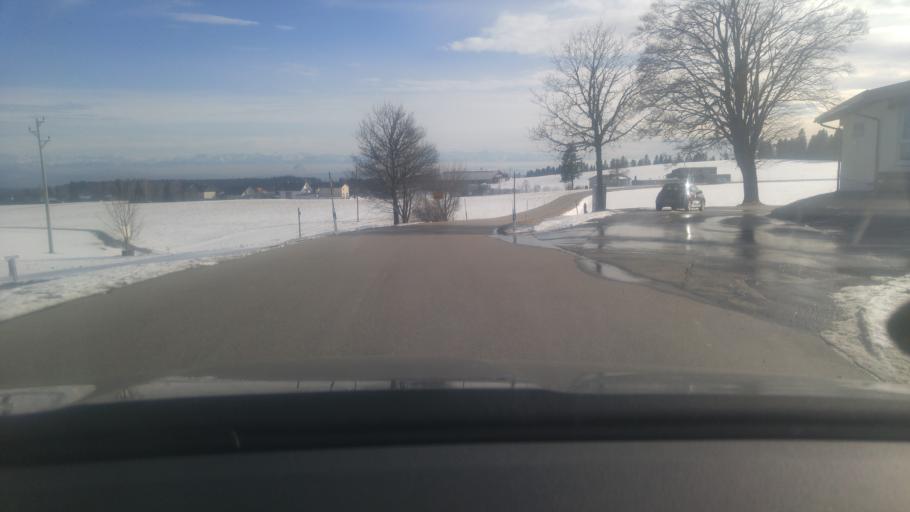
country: DE
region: Baden-Wuerttemberg
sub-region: Freiburg Region
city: Hochenschwand
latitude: 47.7150
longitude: 8.1524
